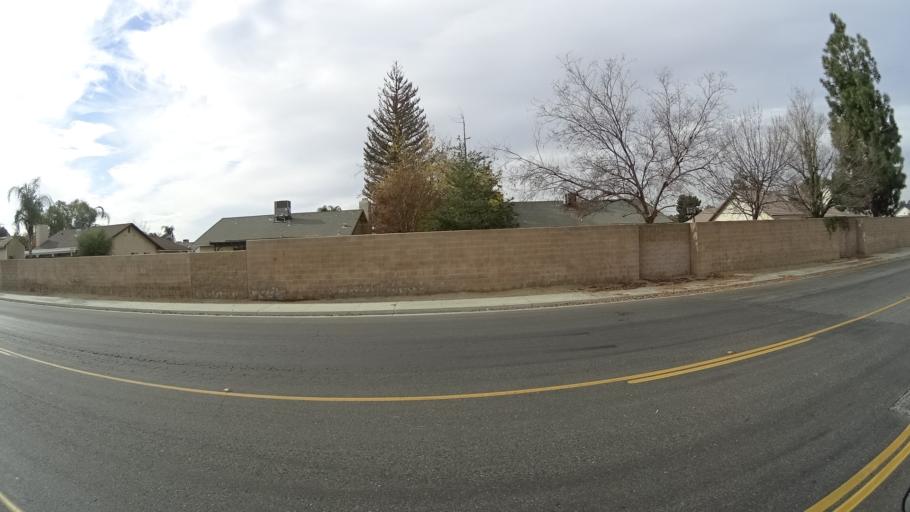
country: US
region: California
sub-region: Kern County
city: Rosedale
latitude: 35.3952
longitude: -119.1367
